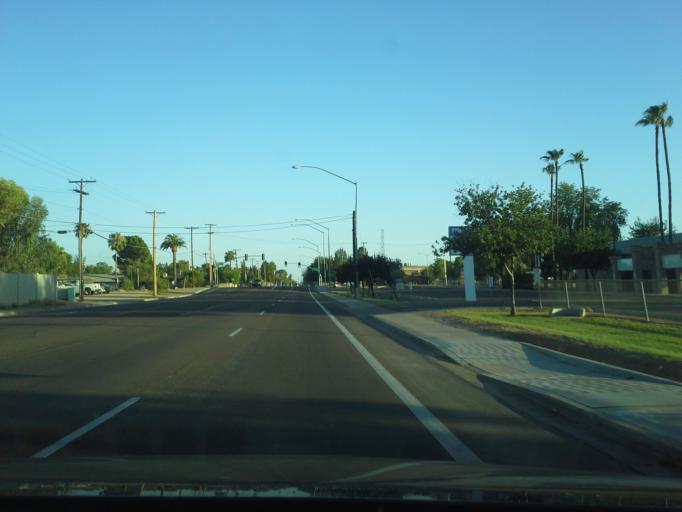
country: US
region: Arizona
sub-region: Maricopa County
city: Mesa
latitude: 33.4316
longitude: -111.8228
